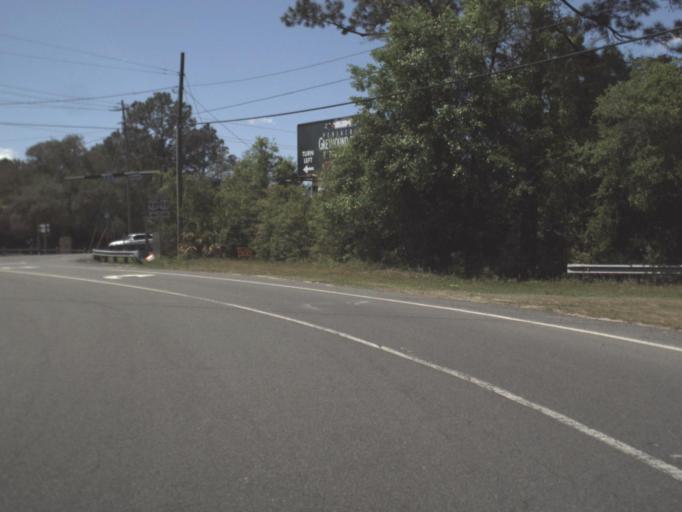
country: US
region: Florida
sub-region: Escambia County
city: Myrtle Grove
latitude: 30.4035
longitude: -87.3740
